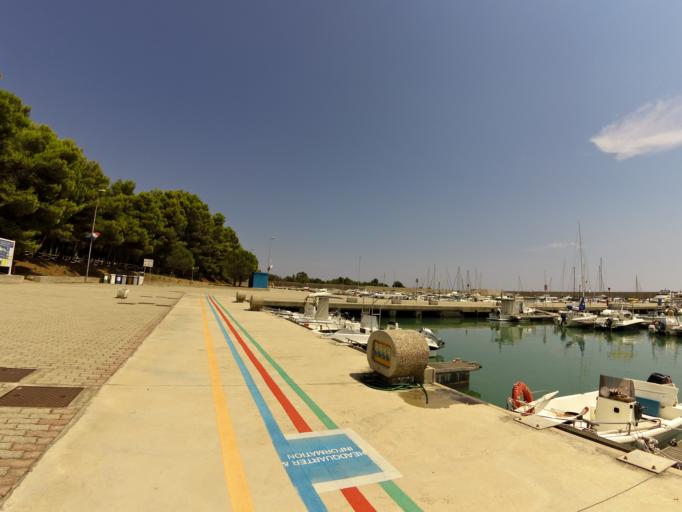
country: IT
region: Calabria
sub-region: Provincia di Reggio Calabria
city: Caulonia Marina
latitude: 38.3290
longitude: 16.4338
